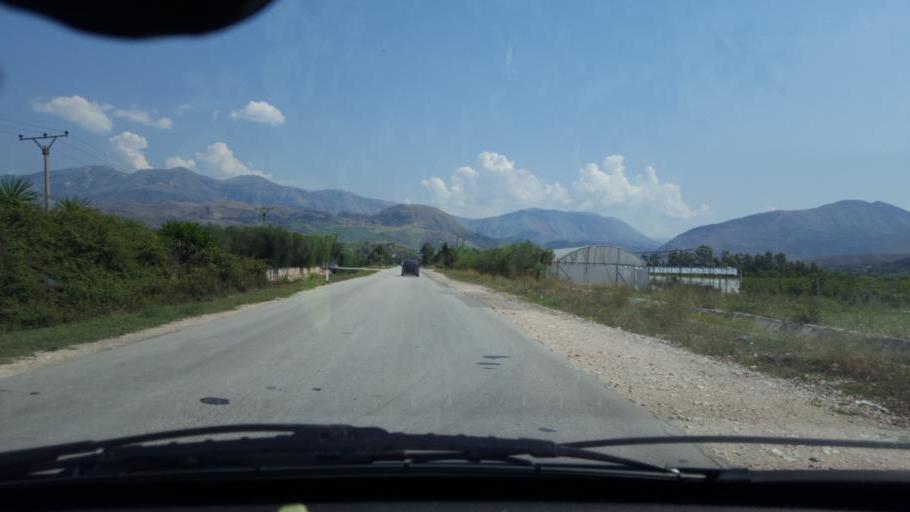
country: AL
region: Vlore
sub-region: Rrethi i Delvines
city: Finiq
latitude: 39.8909
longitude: 20.0652
